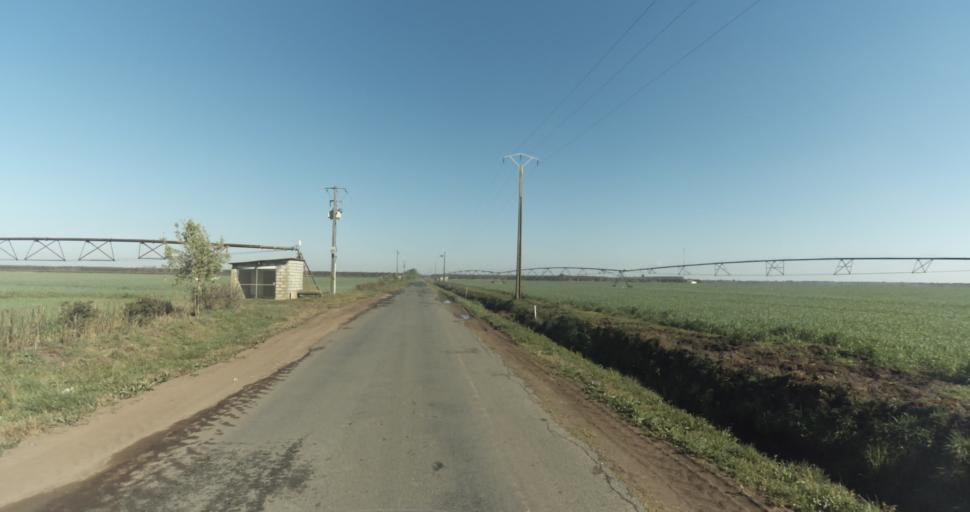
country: FR
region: Aquitaine
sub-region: Departement de la Gironde
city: Marcheprime
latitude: 44.7678
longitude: -0.8555
